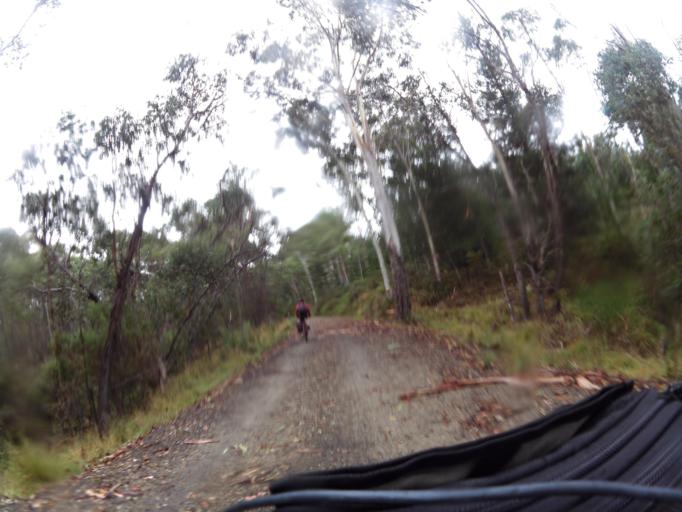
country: AU
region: New South Wales
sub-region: Greater Hume Shire
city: Holbrook
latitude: -36.1750
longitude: 147.5003
